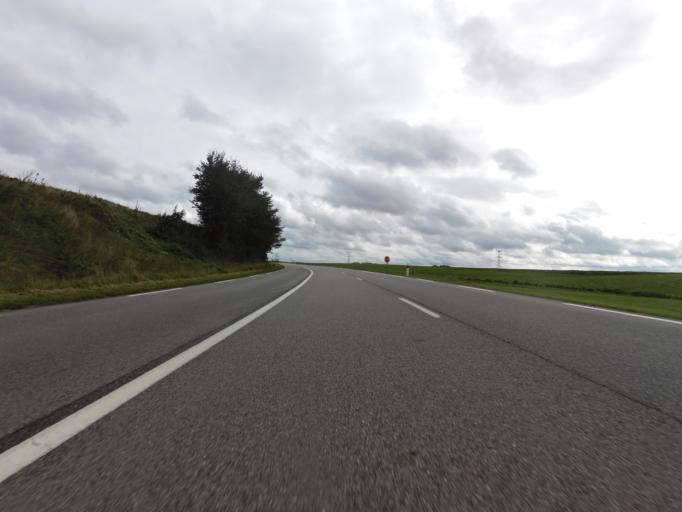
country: FR
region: Haute-Normandie
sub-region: Departement de la Seine-Maritime
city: Criel-sur-Mer
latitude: 50.0190
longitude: 1.3526
